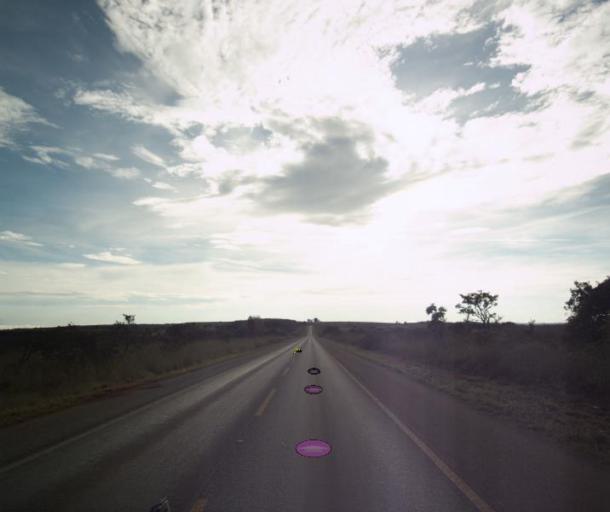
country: BR
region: Goias
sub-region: Pirenopolis
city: Pirenopolis
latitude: -15.7537
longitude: -48.6793
